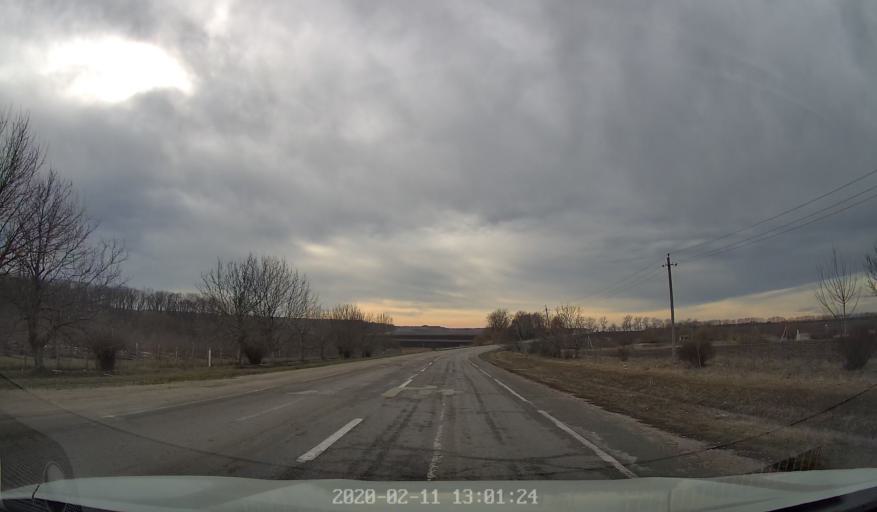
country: MD
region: Briceni
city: Briceni
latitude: 48.3182
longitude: 27.0014
